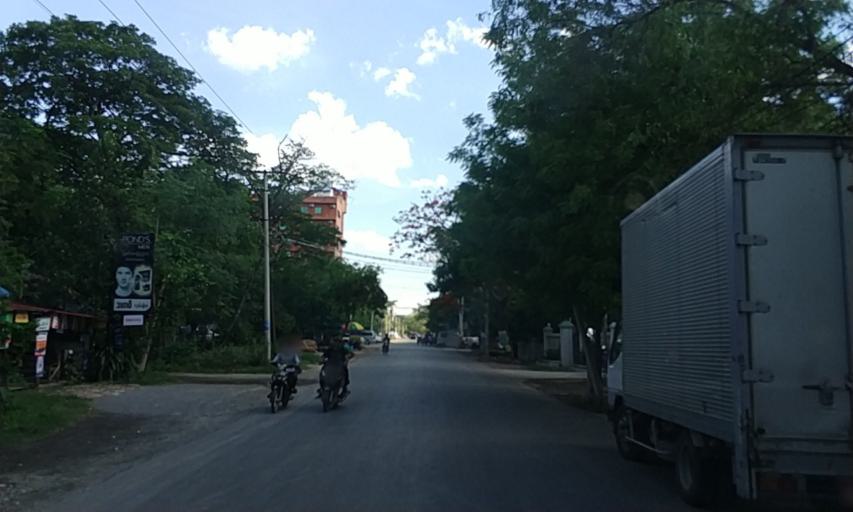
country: MM
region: Mandalay
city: Mandalay
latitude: 21.9746
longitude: 96.1079
